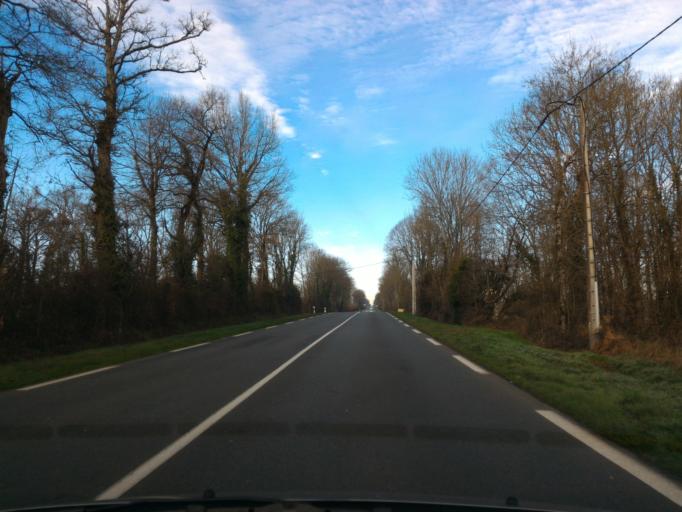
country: FR
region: Poitou-Charentes
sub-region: Departement de la Charente
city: Confolens
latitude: 46.0263
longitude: 0.6497
